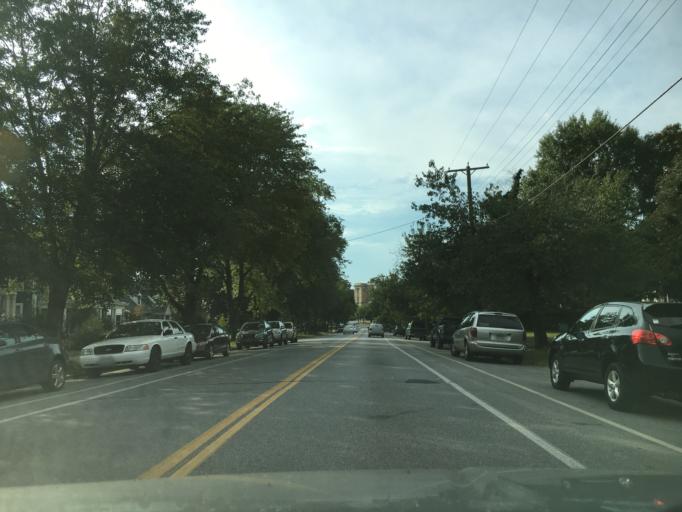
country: US
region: Virginia
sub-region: City of Lynchburg
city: Lynchburg
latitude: 37.4355
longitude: -79.1624
